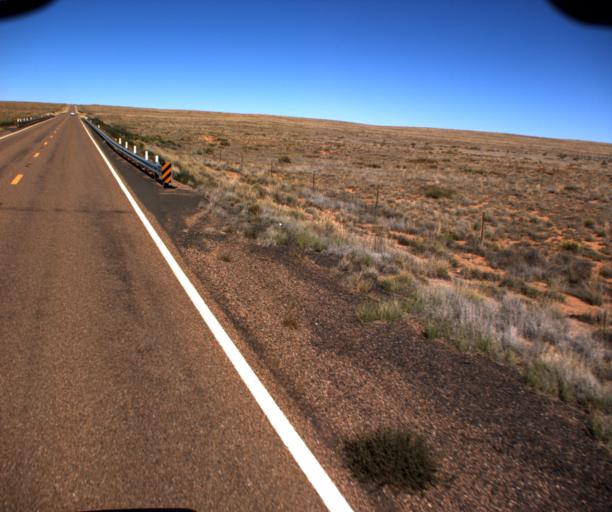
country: US
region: Arizona
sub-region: Navajo County
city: Holbrook
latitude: 34.9891
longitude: -110.0890
